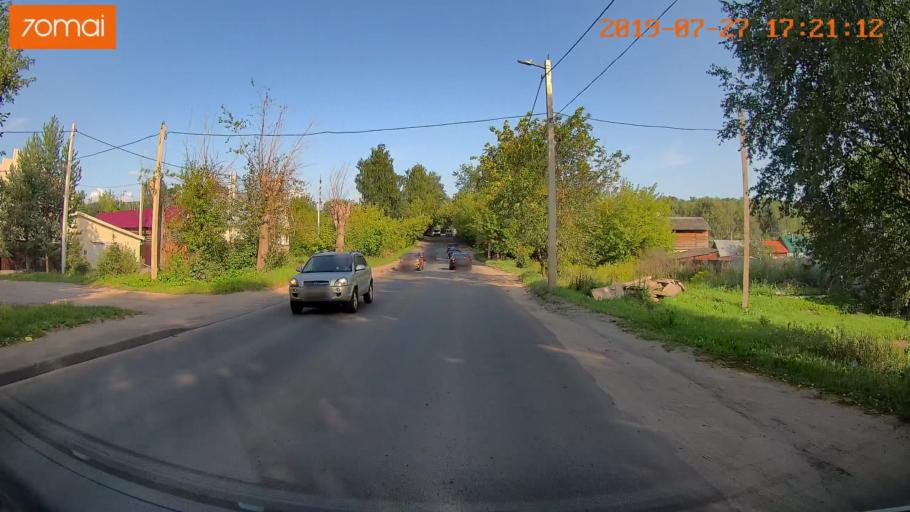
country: RU
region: Ivanovo
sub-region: Gorod Ivanovo
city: Ivanovo
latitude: 57.0280
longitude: 40.9306
